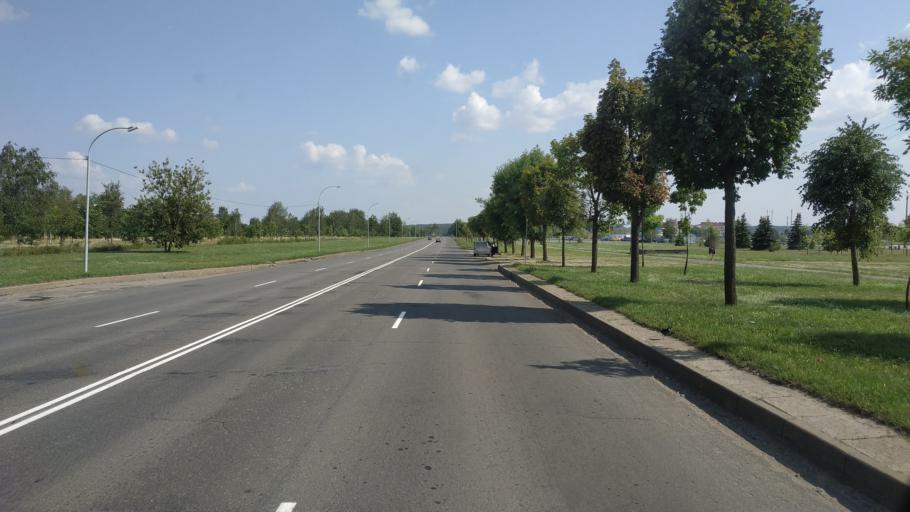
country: BY
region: Mogilev
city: Buynichy
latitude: 53.8624
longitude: 30.3213
